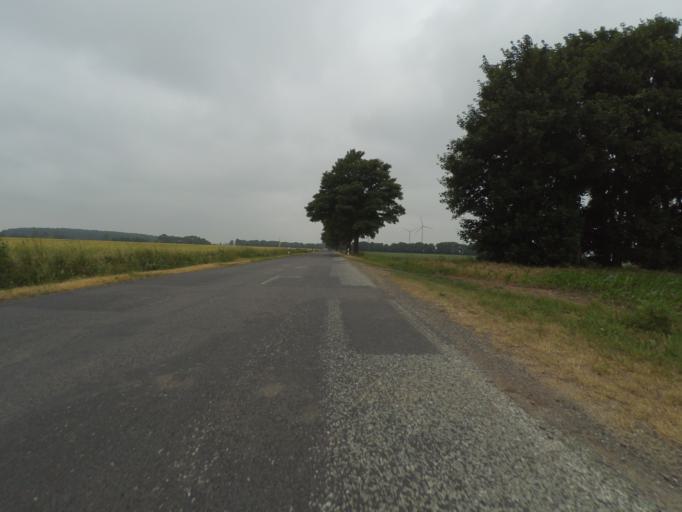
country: DE
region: Mecklenburg-Vorpommern
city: Plau am See
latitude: 53.4911
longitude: 12.2479
